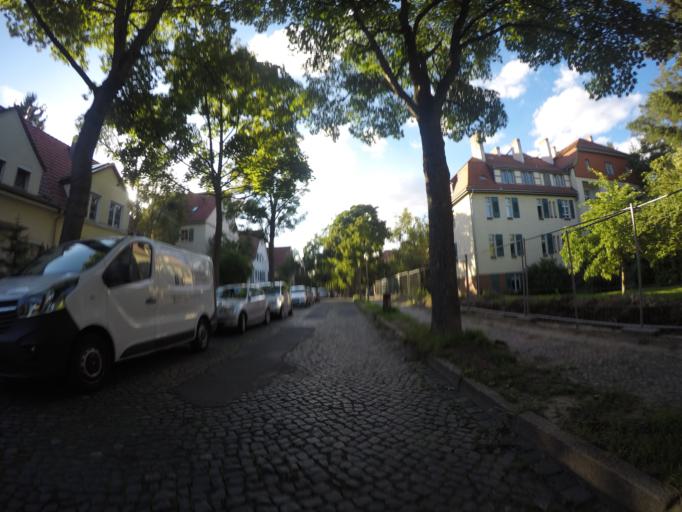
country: DE
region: Berlin
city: Dahlem
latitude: 52.4444
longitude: 13.2881
